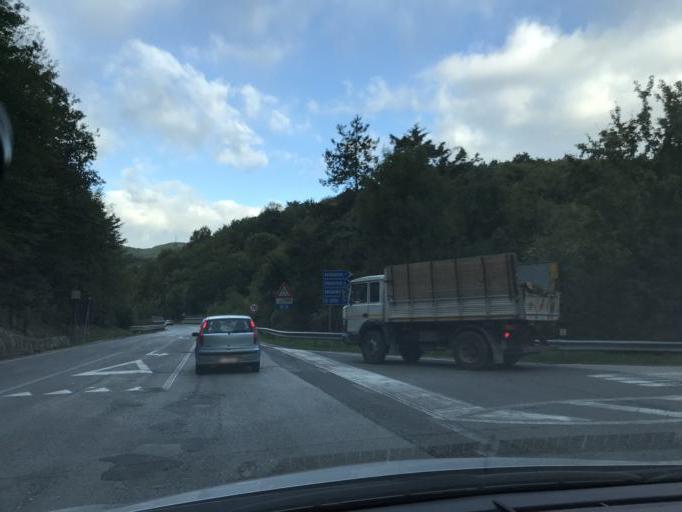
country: IT
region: Umbria
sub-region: Provincia di Terni
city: Ferentillo
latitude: 42.6682
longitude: 12.7340
